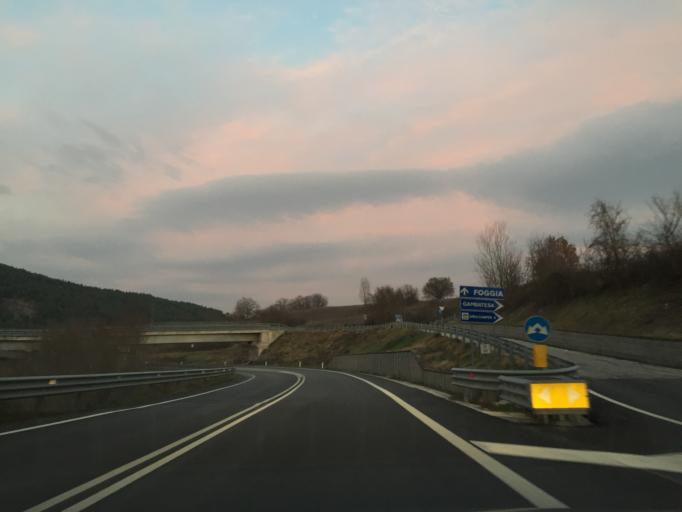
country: IT
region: Molise
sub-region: Provincia di Campobasso
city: Gambatesa
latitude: 41.5254
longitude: 14.9102
